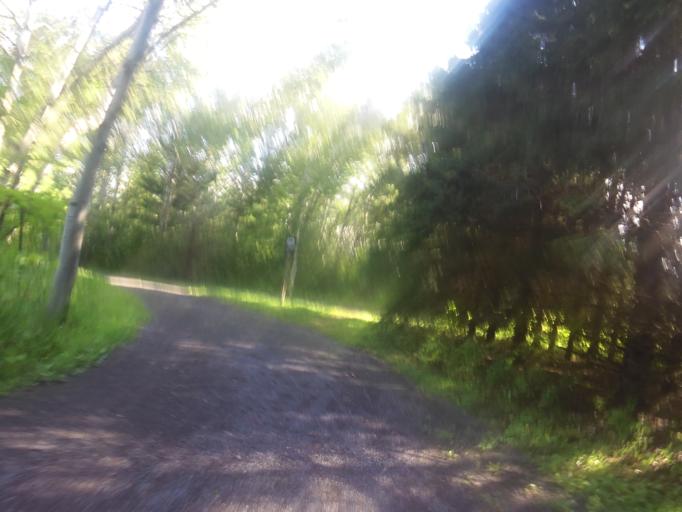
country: CA
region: Ontario
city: Bells Corners
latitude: 45.3274
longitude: -75.7972
